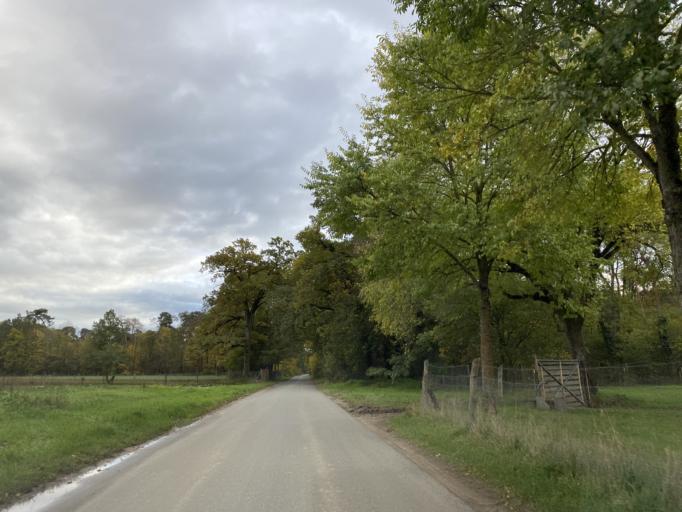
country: DE
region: Hesse
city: Griesheim
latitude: 49.8324
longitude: 8.5770
